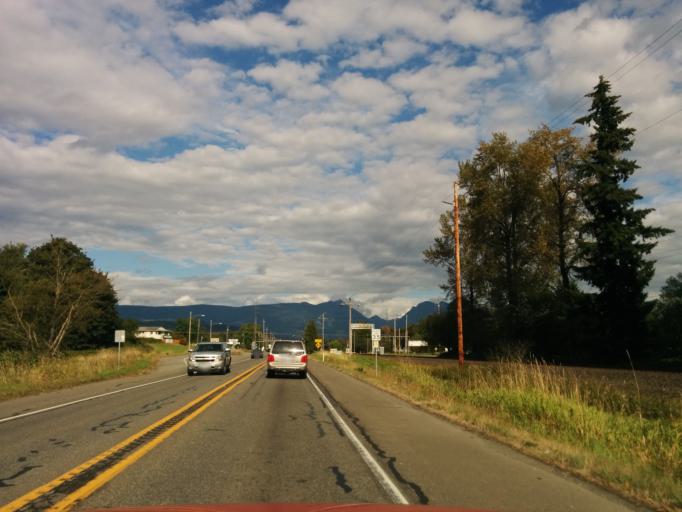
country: US
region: Washington
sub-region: Snohomish County
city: Sultan
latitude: 47.8567
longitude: -121.8353
